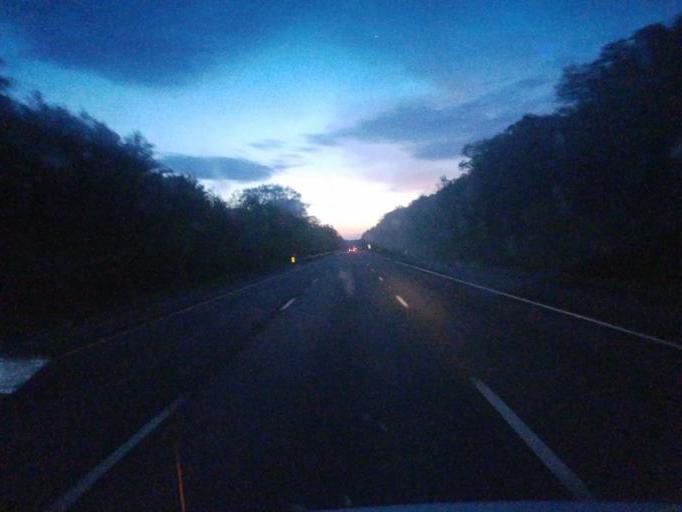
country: US
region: Massachusetts
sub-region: Worcester County
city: Harvard
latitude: 42.4582
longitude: -71.5723
